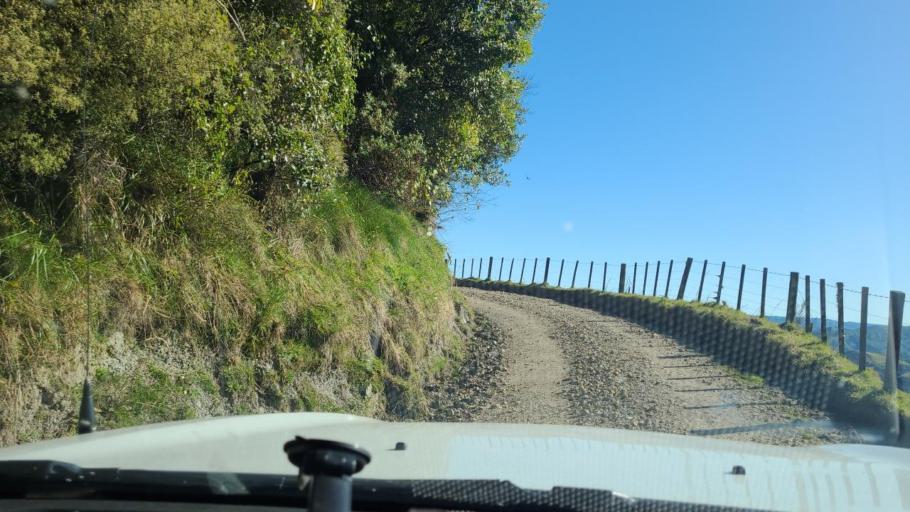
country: NZ
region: Hawke's Bay
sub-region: Wairoa District
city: Wairoa
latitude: -38.6829
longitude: 177.4582
